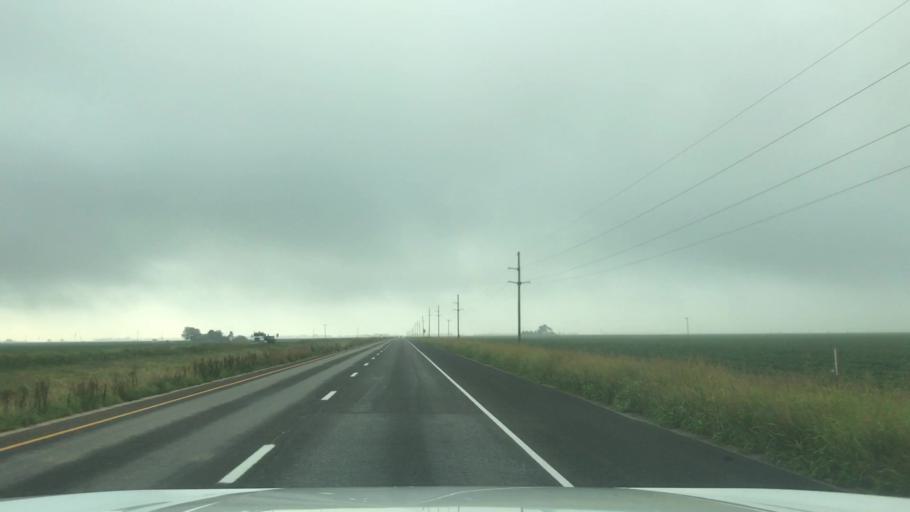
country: US
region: Texas
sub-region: Lubbock County
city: Slaton
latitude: 33.3774
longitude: -101.5812
